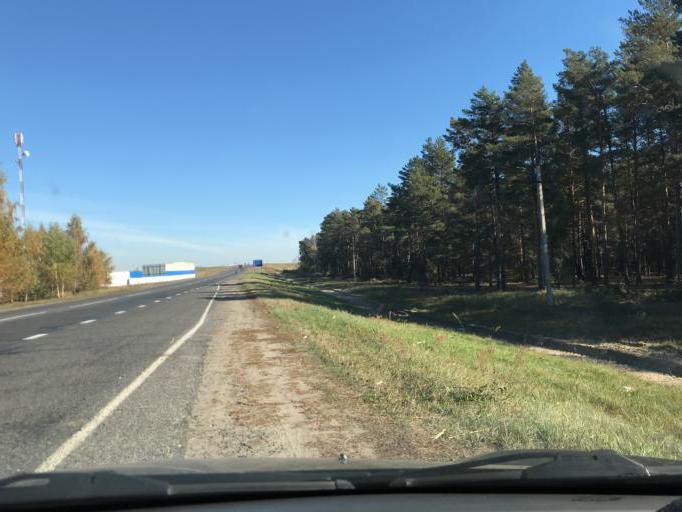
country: BY
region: Gomel
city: Mazyr
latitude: 52.0120
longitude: 29.2626
